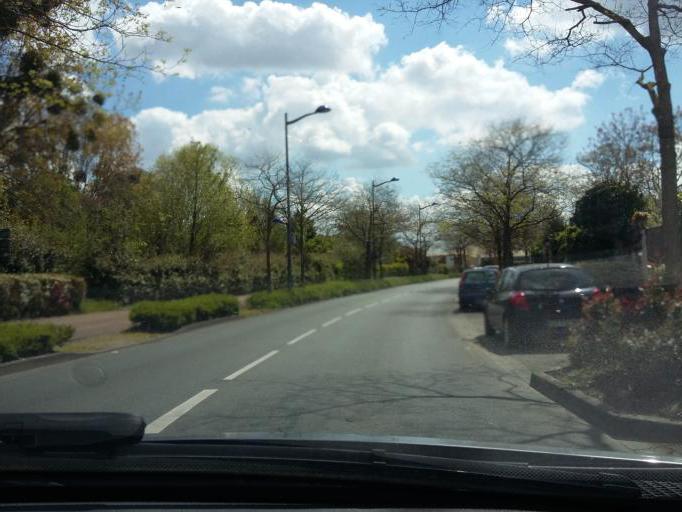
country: FR
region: Ile-de-France
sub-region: Departement du Val-d'Oise
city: Saint-Gratien
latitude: 48.9771
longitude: 2.2716
